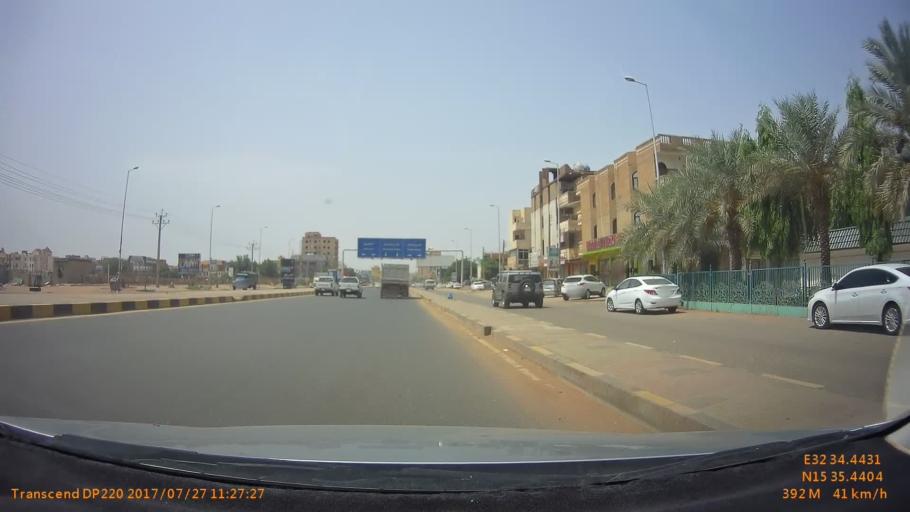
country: SD
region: Khartoum
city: Khartoum
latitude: 15.5906
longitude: 32.5741
